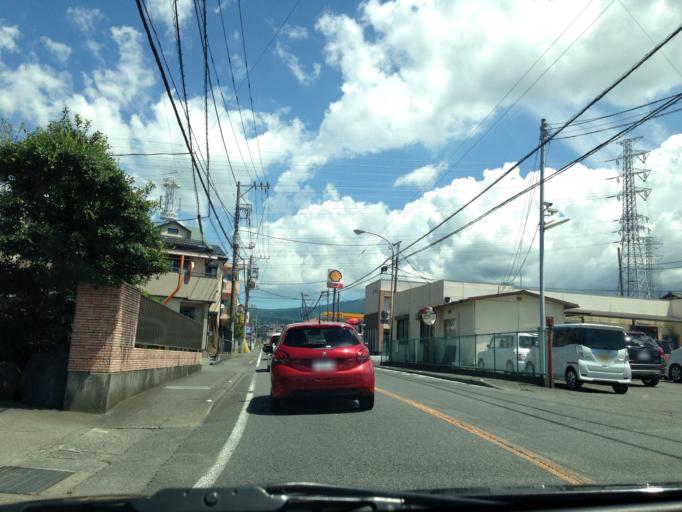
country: JP
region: Shizuoka
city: Fuji
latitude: 35.1736
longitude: 138.6912
